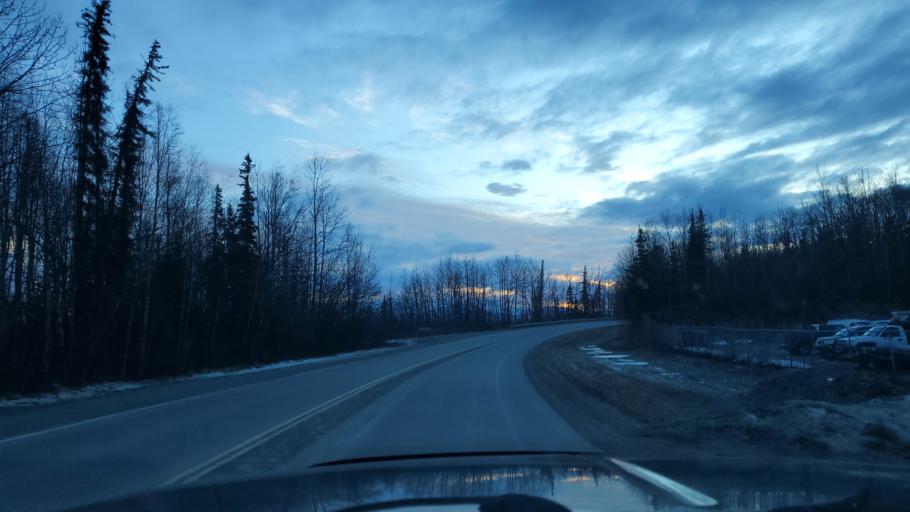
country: US
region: Alaska
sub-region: Matanuska-Susitna Borough
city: Lakes
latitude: 61.6109
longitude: -149.3305
